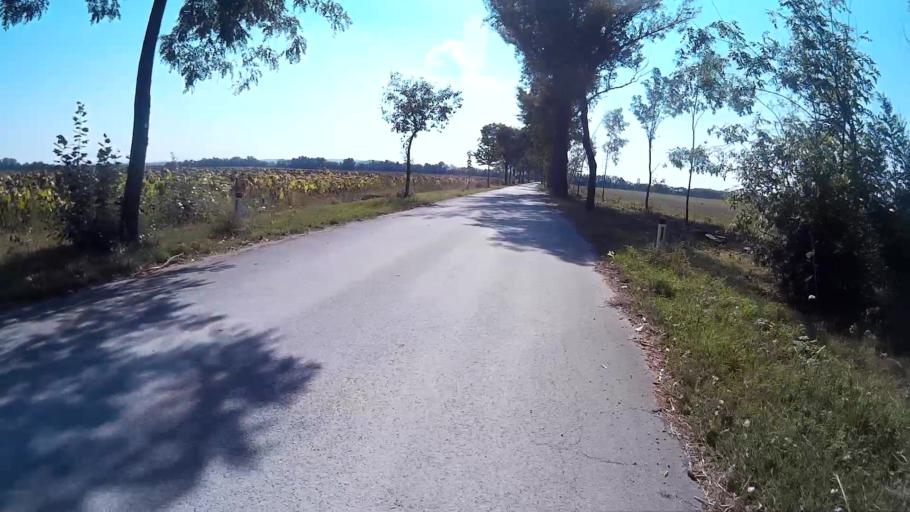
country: CZ
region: South Moravian
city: Novosedly
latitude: 48.7928
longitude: 16.4891
